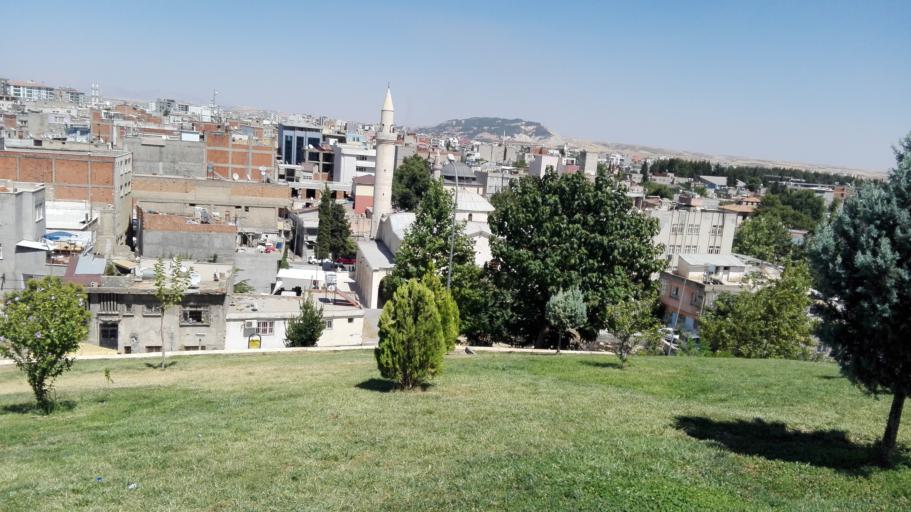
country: TR
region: Adiyaman
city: Adiyaman
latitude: 37.7595
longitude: 38.2762
